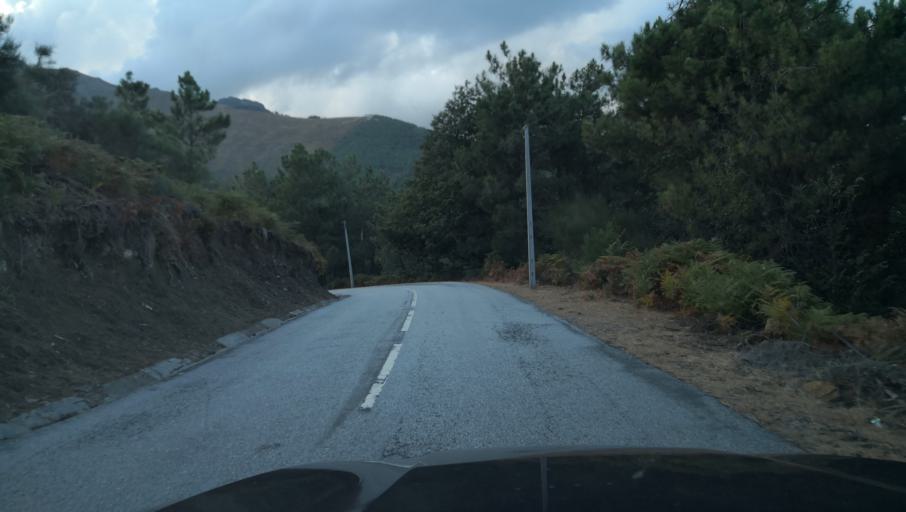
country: PT
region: Vila Real
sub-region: Santa Marta de Penaguiao
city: Santa Marta de Penaguiao
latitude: 41.2371
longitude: -7.8450
